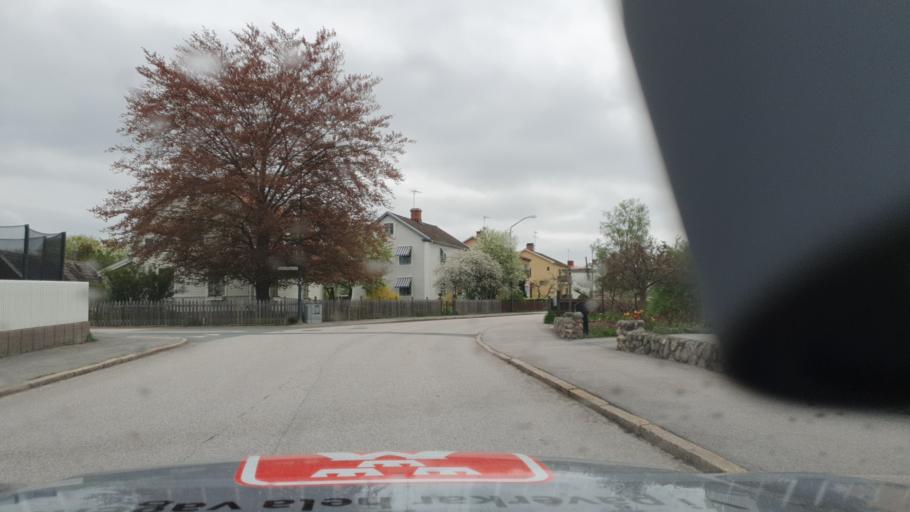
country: SE
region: Kalmar
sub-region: Vimmerby Kommun
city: Vimmerby
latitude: 57.6703
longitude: 15.8644
